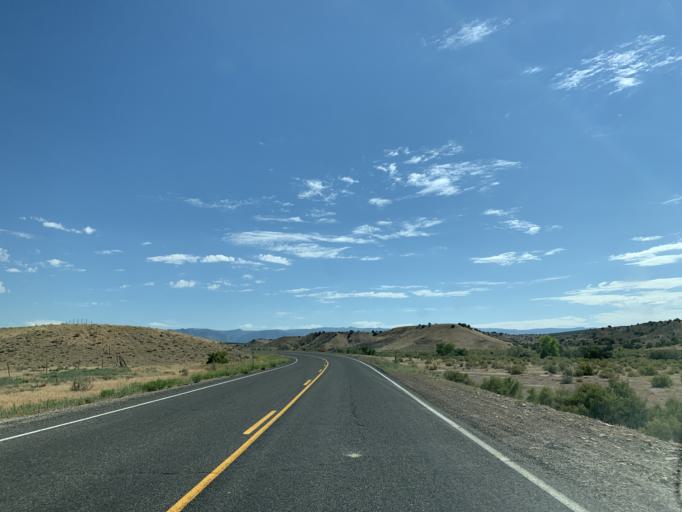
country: US
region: Utah
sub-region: Carbon County
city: Wellington
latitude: 39.5608
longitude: -110.6591
